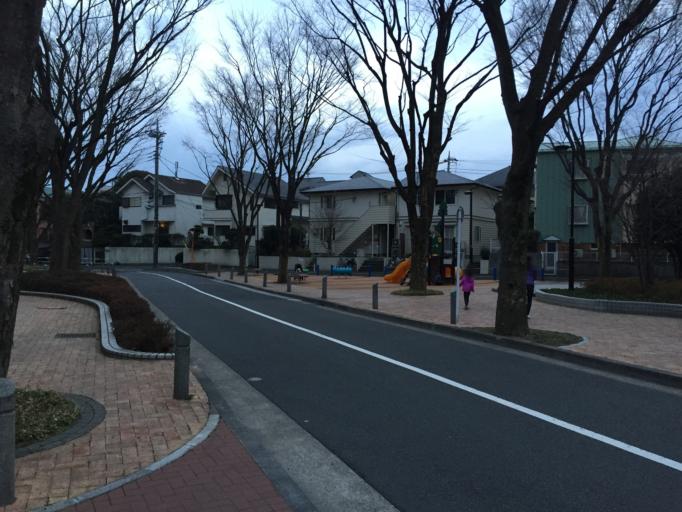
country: JP
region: Tokyo
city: Tokyo
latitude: 35.6588
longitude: 139.6329
